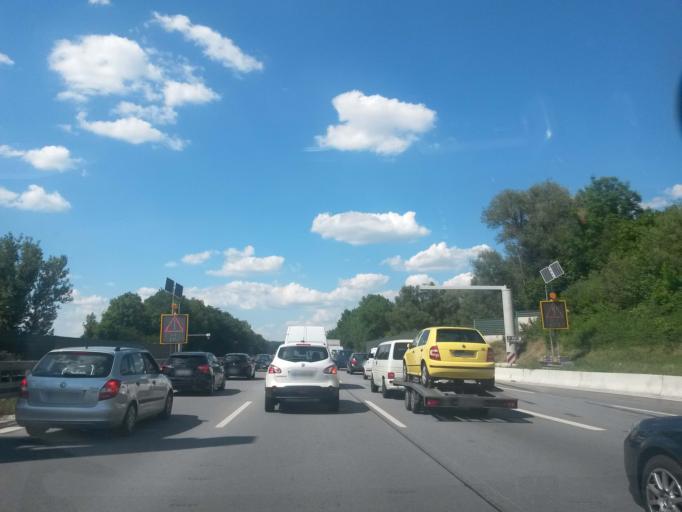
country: DE
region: Bavaria
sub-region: Upper Bavaria
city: Allershausen
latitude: 48.4298
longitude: 11.5895
